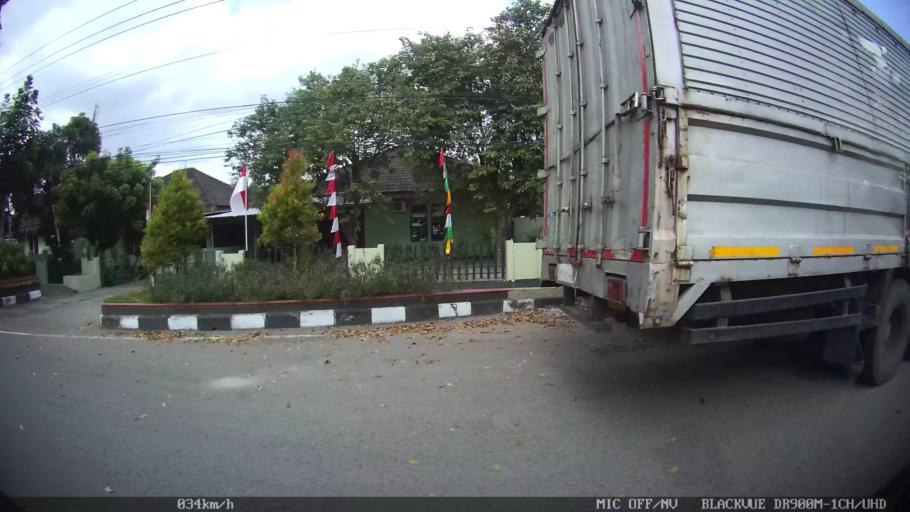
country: ID
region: Daerah Istimewa Yogyakarta
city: Gamping Lor
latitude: -7.7760
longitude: 110.3323
